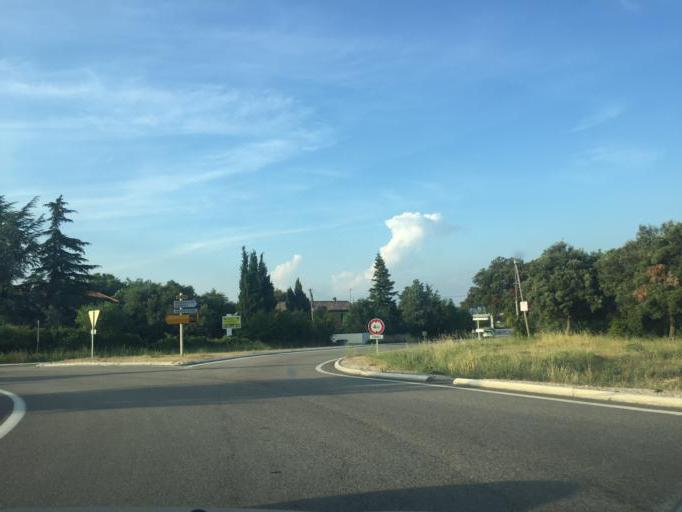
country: FR
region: Languedoc-Roussillon
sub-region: Departement du Gard
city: Pujaut
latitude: 44.0205
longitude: 4.7409
